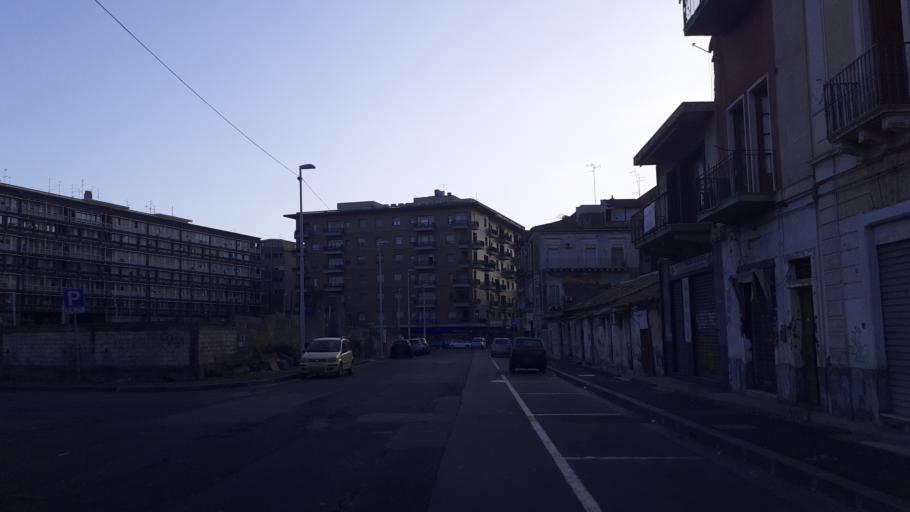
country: IT
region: Sicily
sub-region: Catania
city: Catania
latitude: 37.5092
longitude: 15.0920
